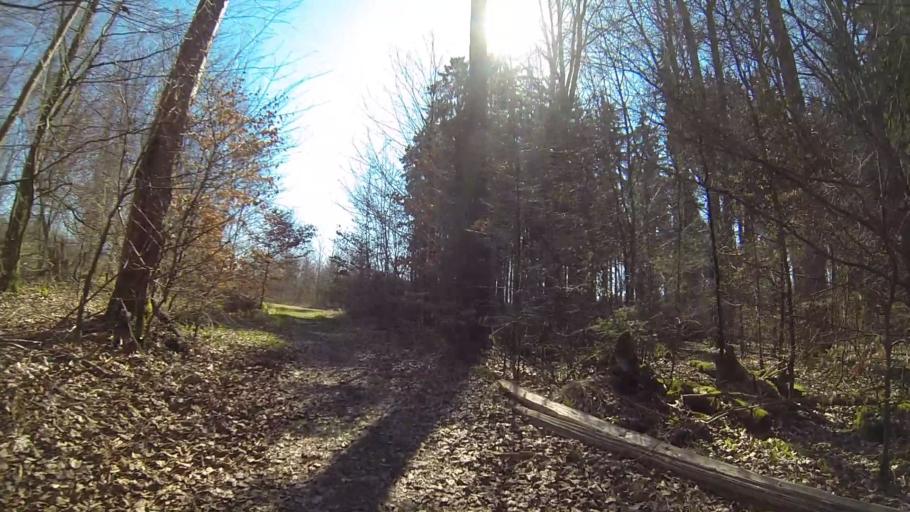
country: DE
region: Baden-Wuerttemberg
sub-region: Regierungsbezirk Stuttgart
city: Heidenheim an der Brenz
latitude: 48.6712
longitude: 10.1956
